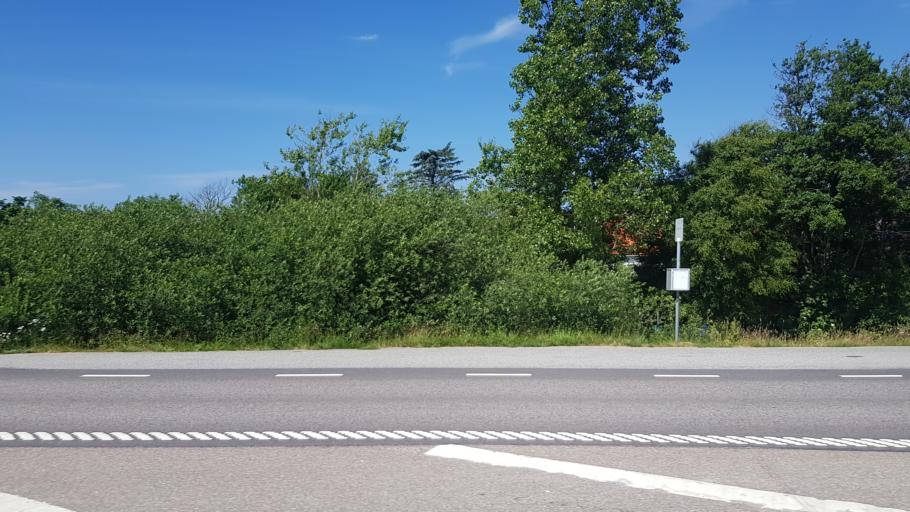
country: SE
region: Vaestra Goetaland
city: Ronnang
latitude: 57.9590
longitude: 11.5835
